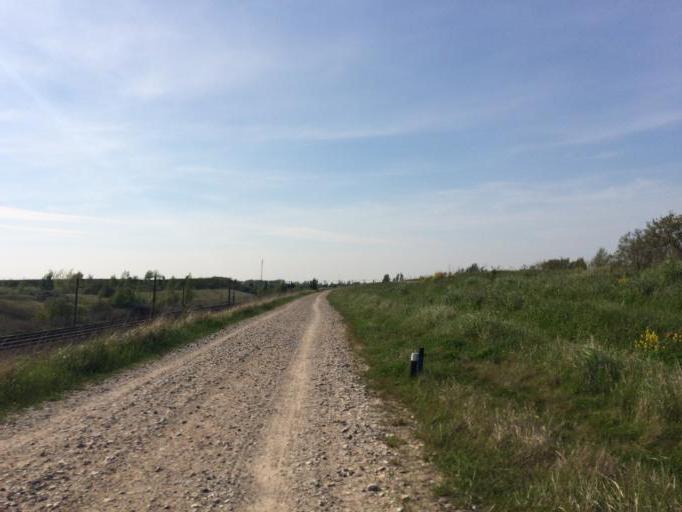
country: DK
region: Capital Region
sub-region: Tarnby Kommune
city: Tarnby
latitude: 55.6320
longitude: 12.5620
